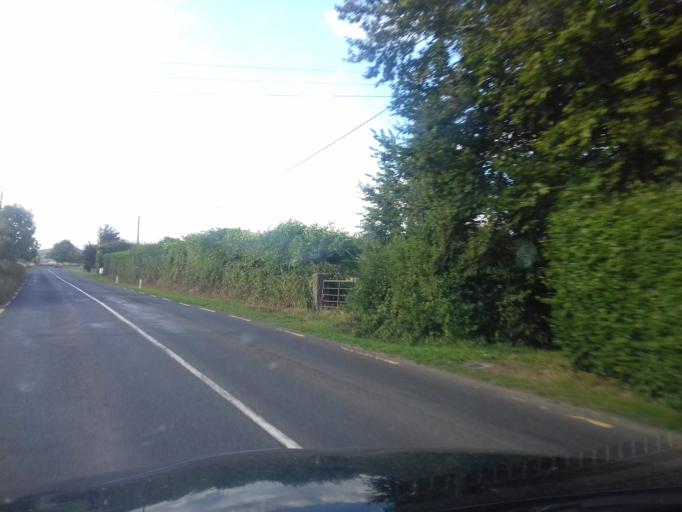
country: IE
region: Leinster
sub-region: Loch Garman
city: New Ross
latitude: 52.4478
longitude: -6.9624
